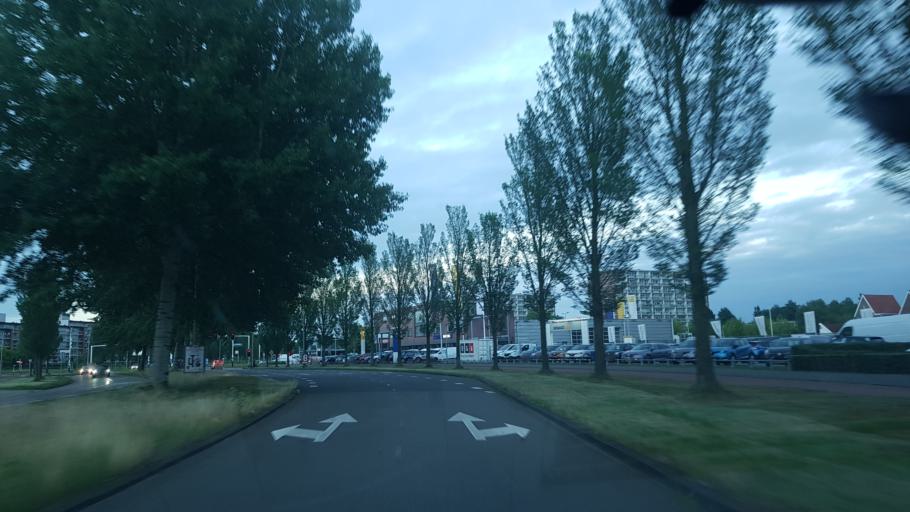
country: NL
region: Friesland
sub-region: Gemeente Leeuwarden
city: Leeuwarden
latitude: 53.2125
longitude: 5.8108
